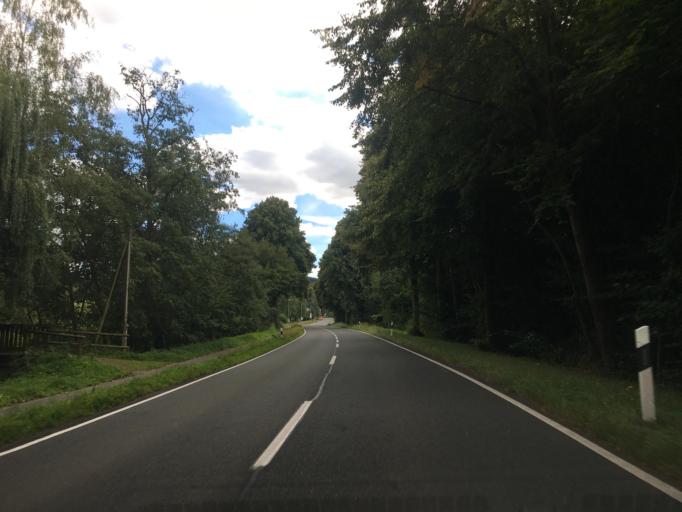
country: DE
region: Lower Saxony
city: Vahlbruch
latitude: 52.0057
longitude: 9.3372
